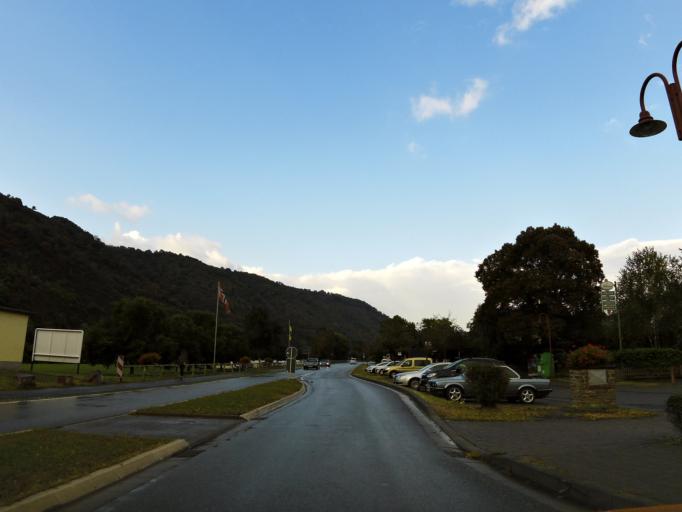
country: DE
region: Rheinland-Pfalz
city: Burgen
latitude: 50.2122
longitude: 7.3881
